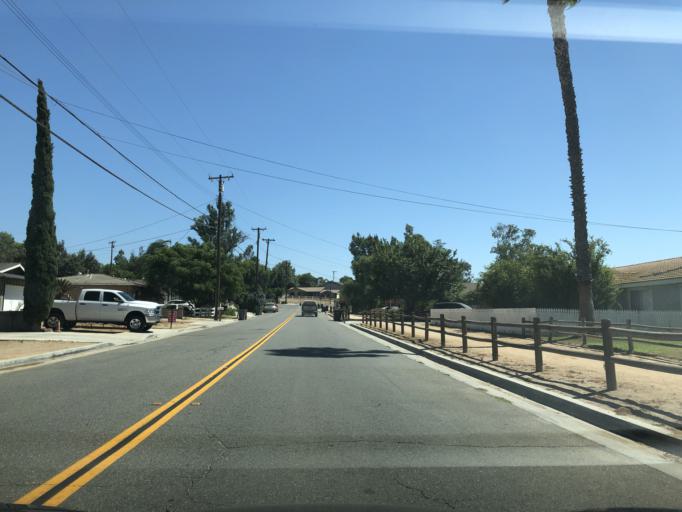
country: US
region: California
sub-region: Riverside County
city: Norco
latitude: 33.9196
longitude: -117.5542
